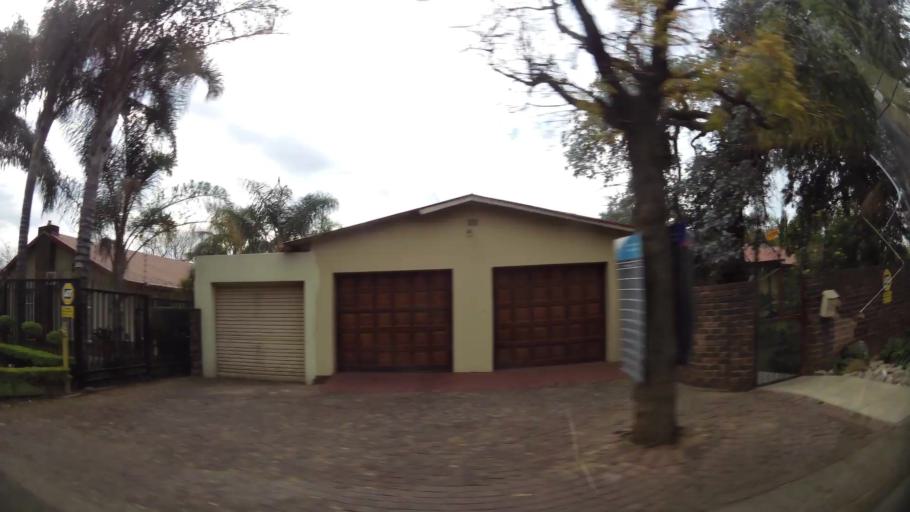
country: ZA
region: Gauteng
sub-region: City of Tshwane Metropolitan Municipality
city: Pretoria
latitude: -25.7160
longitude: 28.3207
